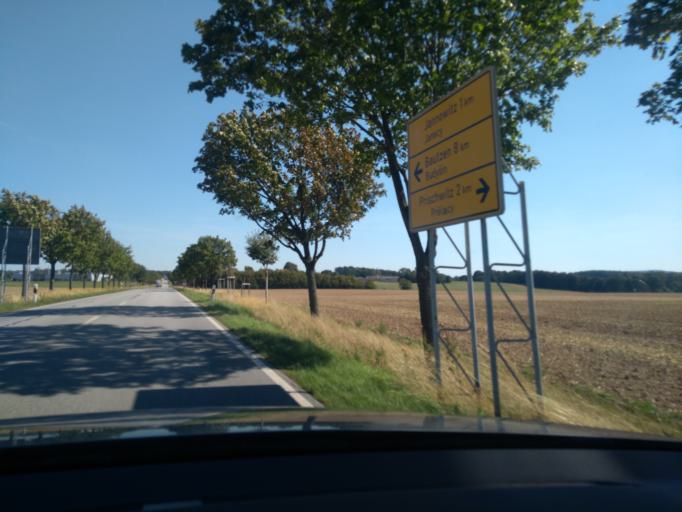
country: DE
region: Saxony
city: Goda
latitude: 51.1951
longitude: 14.3314
